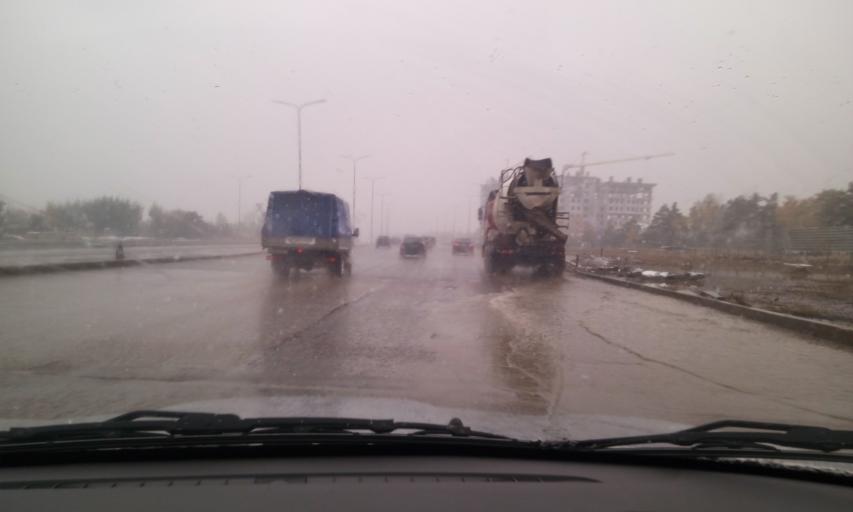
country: KZ
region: Astana Qalasy
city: Astana
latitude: 51.1488
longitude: 71.3689
